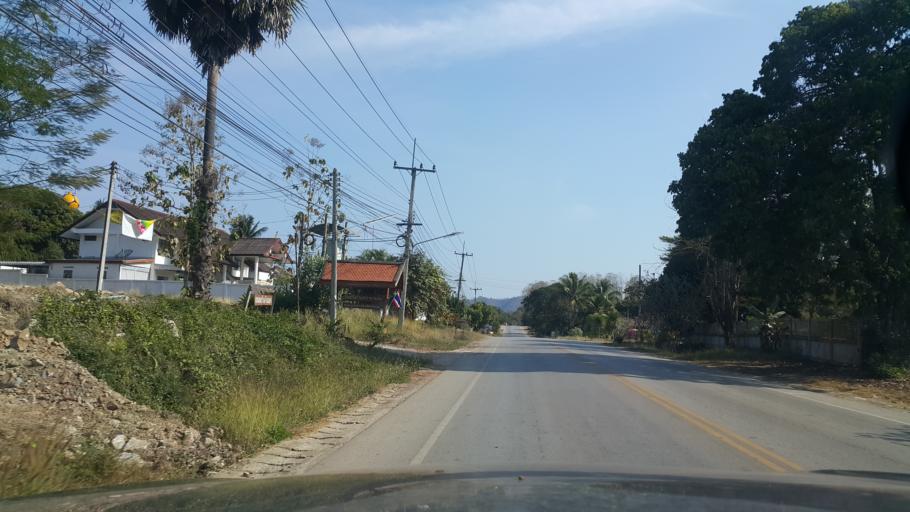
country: LA
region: Vientiane
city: Muang Sanakham
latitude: 17.9091
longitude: 101.7297
